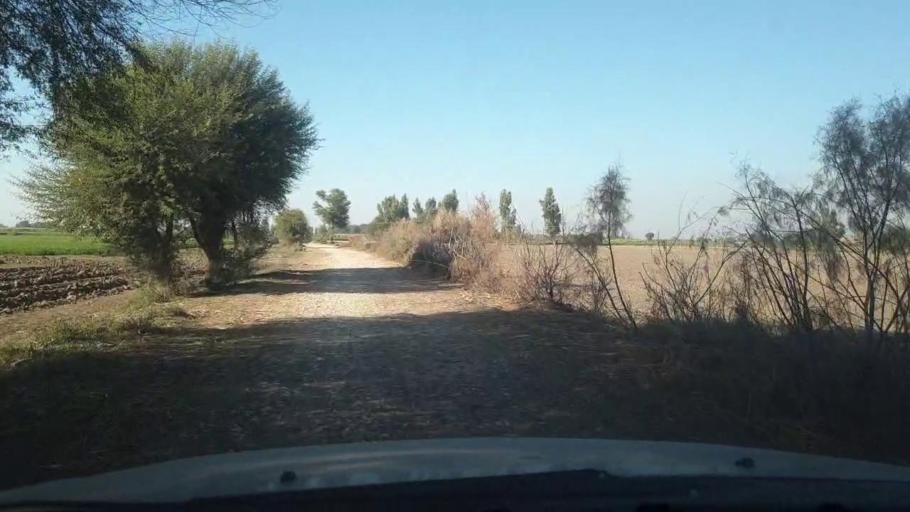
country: PK
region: Sindh
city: Pano Aqil
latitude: 27.9771
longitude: 69.1712
